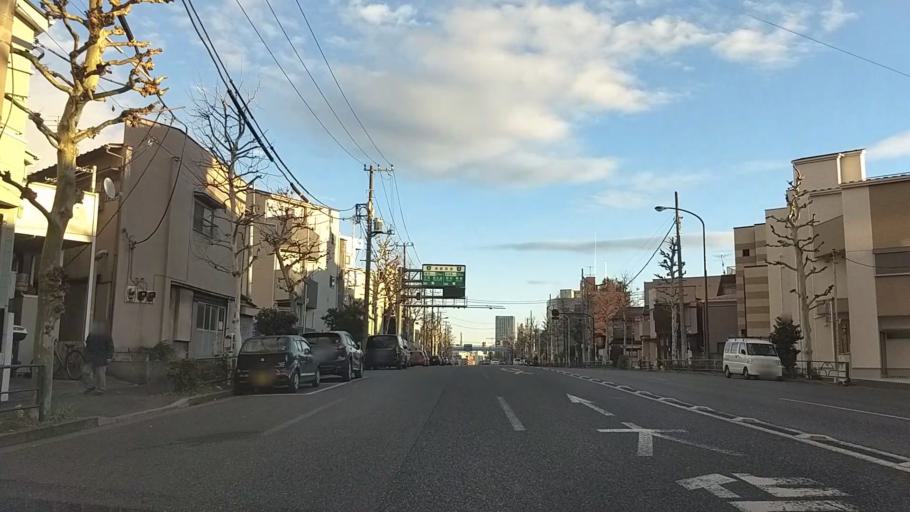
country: JP
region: Tokyo
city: Tokyo
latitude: 35.7223
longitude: 139.6846
